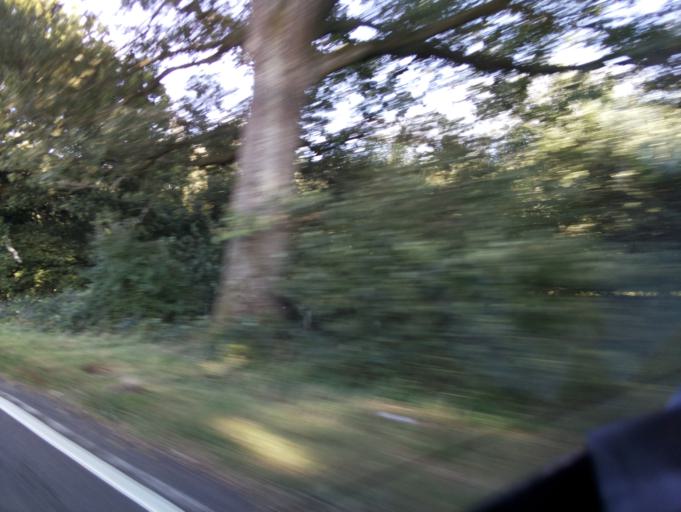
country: GB
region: England
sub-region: Hampshire
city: Four Marks
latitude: 51.0462
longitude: -1.0543
